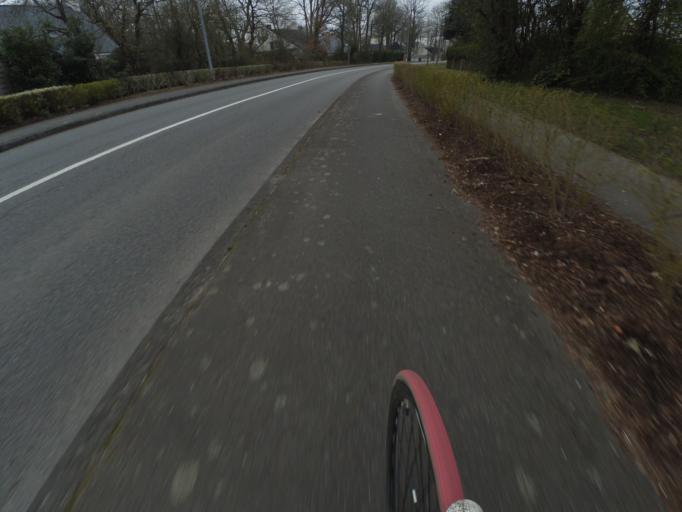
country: FR
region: Pays de la Loire
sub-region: Departement de la Loire-Atlantique
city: Sainte-Luce-sur-Loire
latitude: 47.2740
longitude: -1.4834
